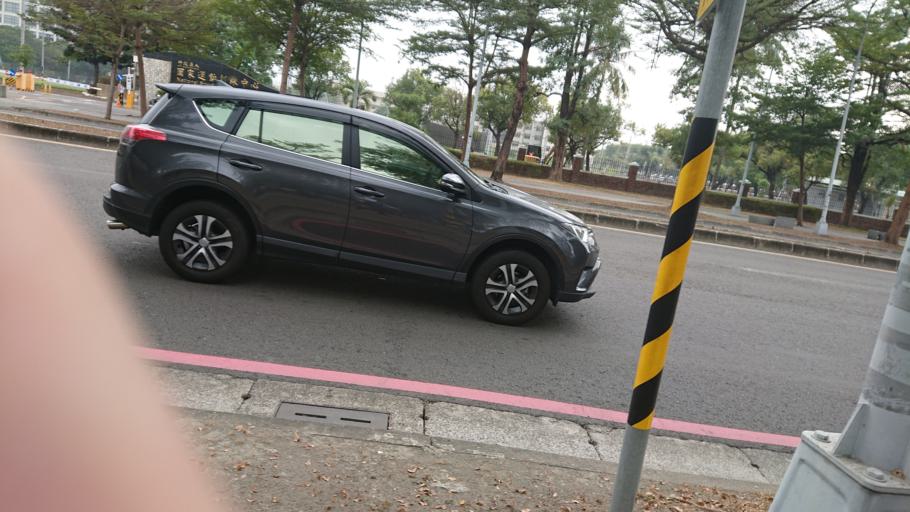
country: TW
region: Kaohsiung
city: Kaohsiung
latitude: 22.7009
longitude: 120.2933
